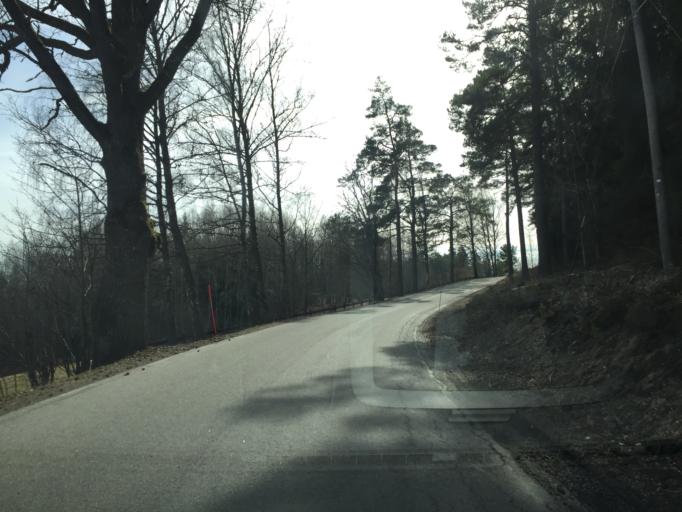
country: SE
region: Stockholm
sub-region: Botkyrka Kommun
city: Tullinge
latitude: 59.1065
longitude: 17.9748
